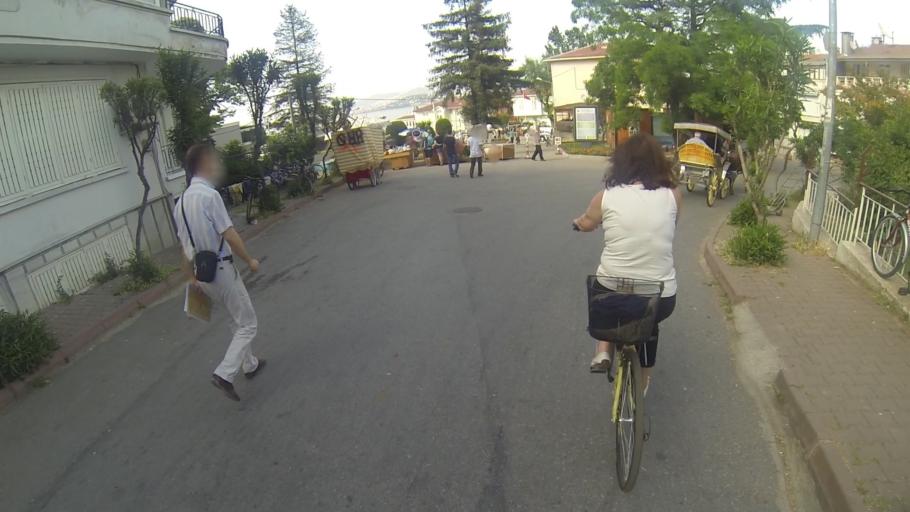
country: TR
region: Istanbul
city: Adalar
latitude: 40.8730
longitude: 29.1273
